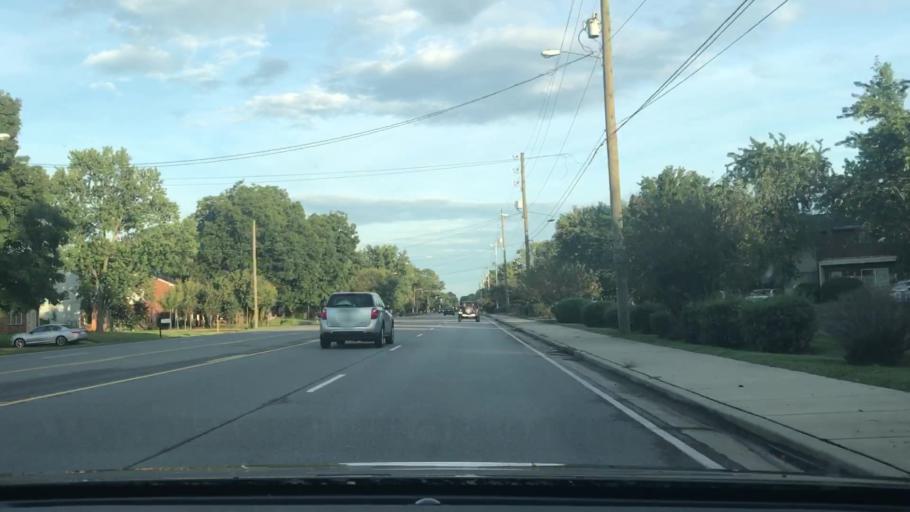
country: US
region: Tennessee
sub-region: Davidson County
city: Oak Hill
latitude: 36.0805
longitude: -86.7506
